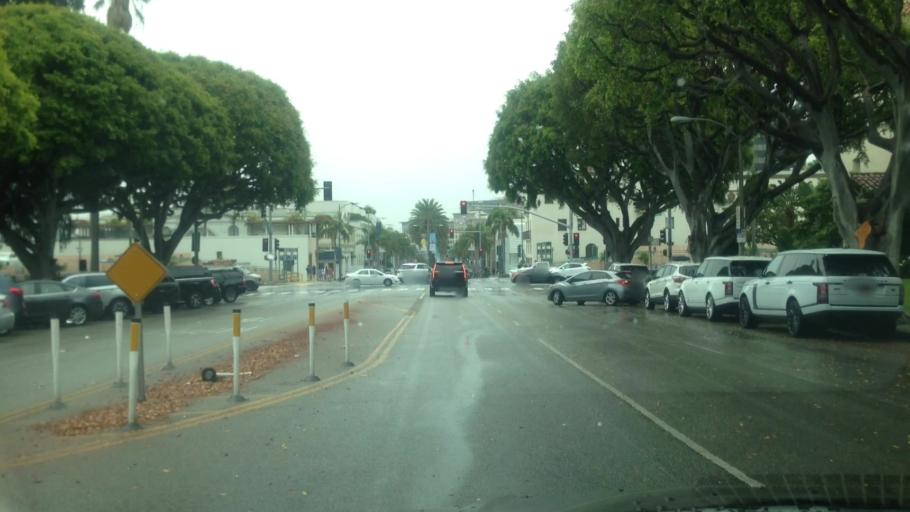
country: US
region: California
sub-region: Los Angeles County
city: Beverly Hills
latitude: 34.0716
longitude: -118.4054
